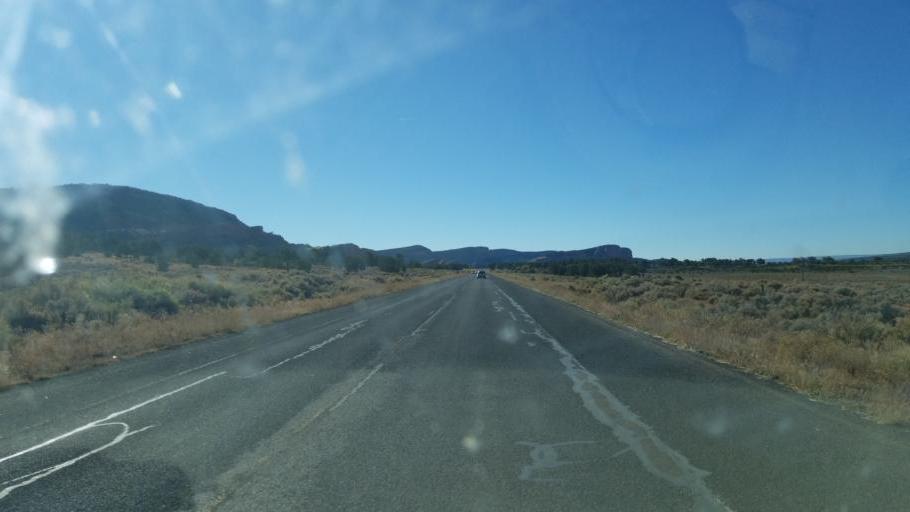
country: US
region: New Mexico
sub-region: McKinley County
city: Navajo
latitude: 35.8742
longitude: -109.0235
